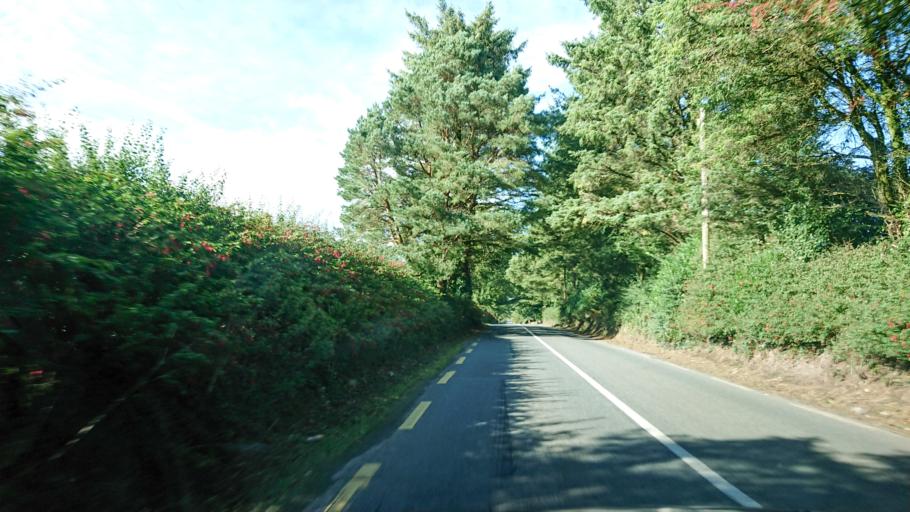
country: IE
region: Munster
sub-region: Waterford
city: Dungarvan
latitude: 52.1950
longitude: -7.6989
